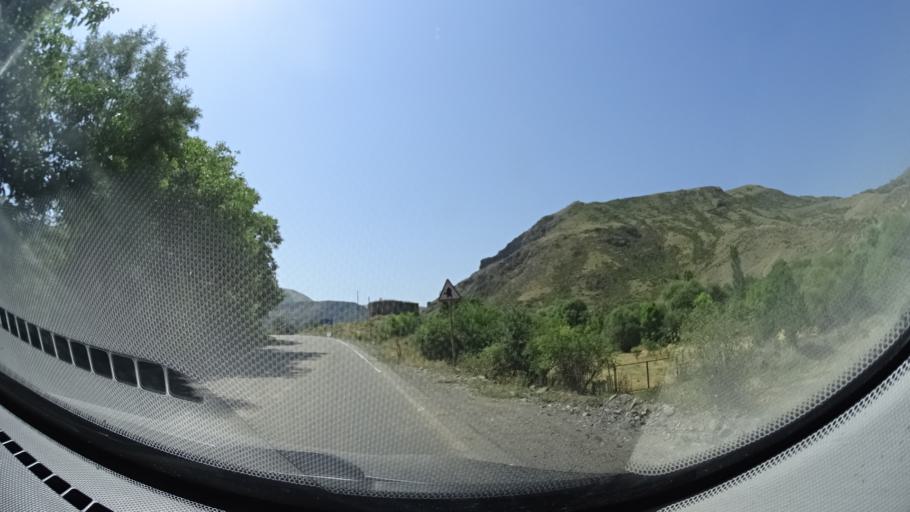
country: GE
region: Samtskhe-Javakheti
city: Aspindza
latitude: 41.4985
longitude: 43.2633
